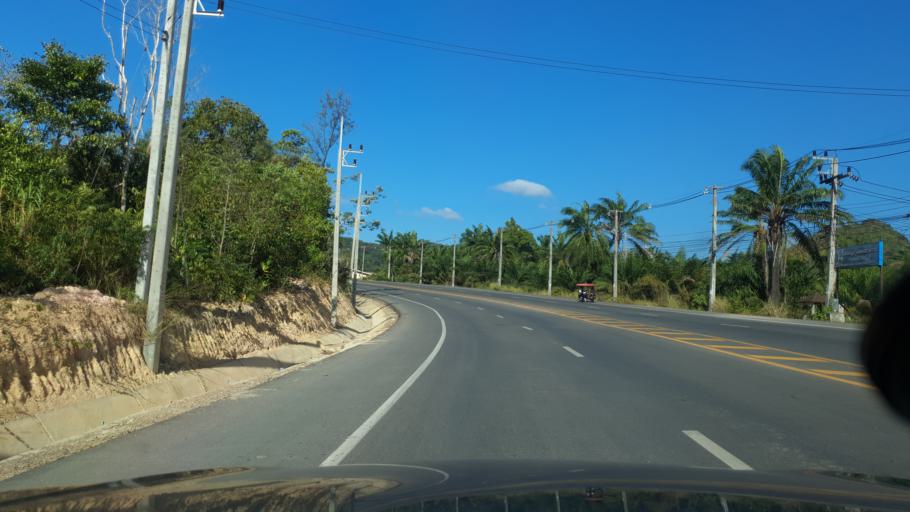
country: TH
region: Phangnga
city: Ban Ao Nang
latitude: 8.0417
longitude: 98.8480
